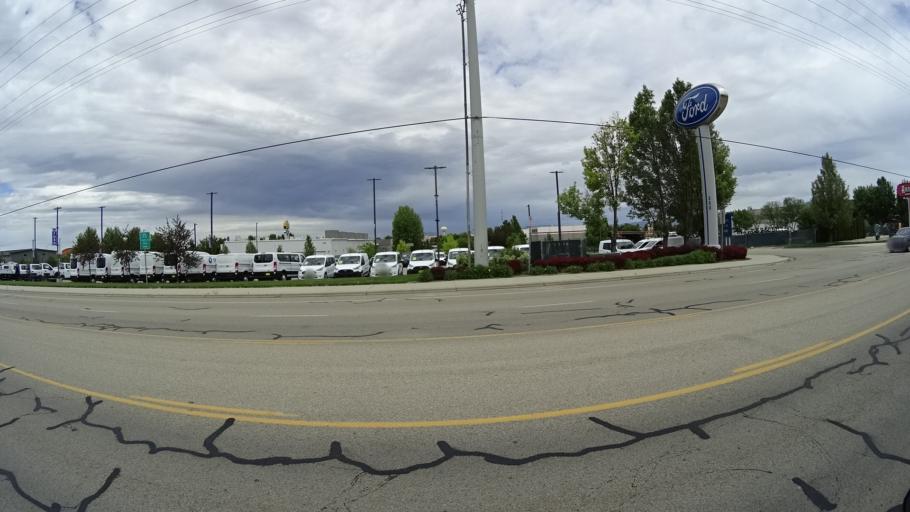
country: US
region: Idaho
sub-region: Ada County
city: Meridian
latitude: 43.5901
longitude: -116.3898
